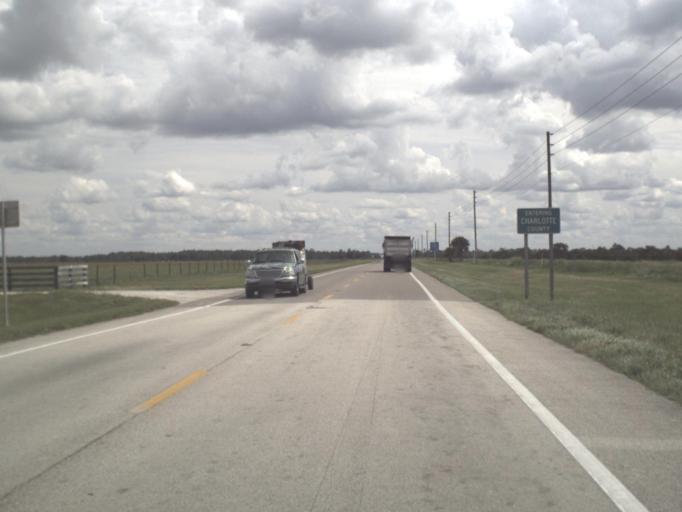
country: US
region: Florida
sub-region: DeSoto County
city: Nocatee
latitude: 27.0341
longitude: -81.7719
